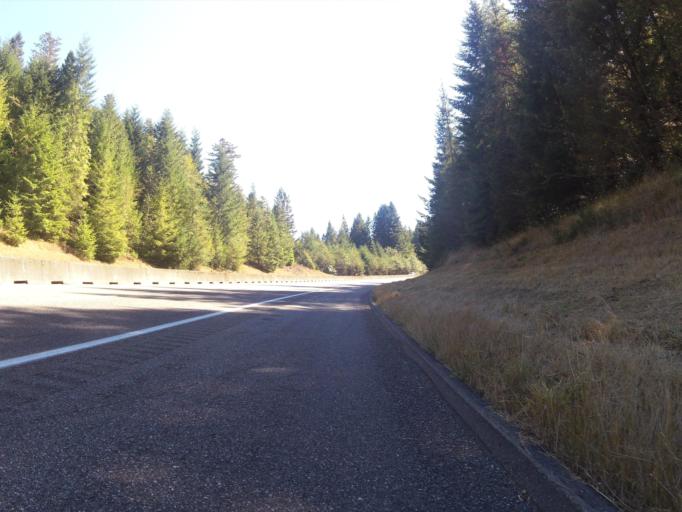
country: US
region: California
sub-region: Humboldt County
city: Westhaven-Moonstone
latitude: 41.4017
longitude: -123.9933
